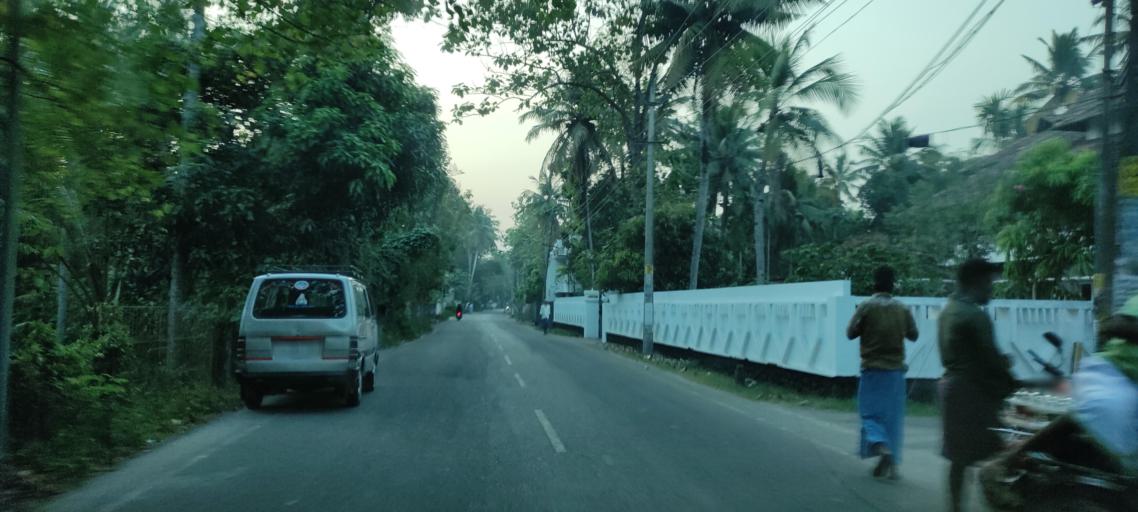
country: IN
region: Kerala
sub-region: Alappuzha
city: Kayankulam
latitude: 9.1252
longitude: 76.4992
